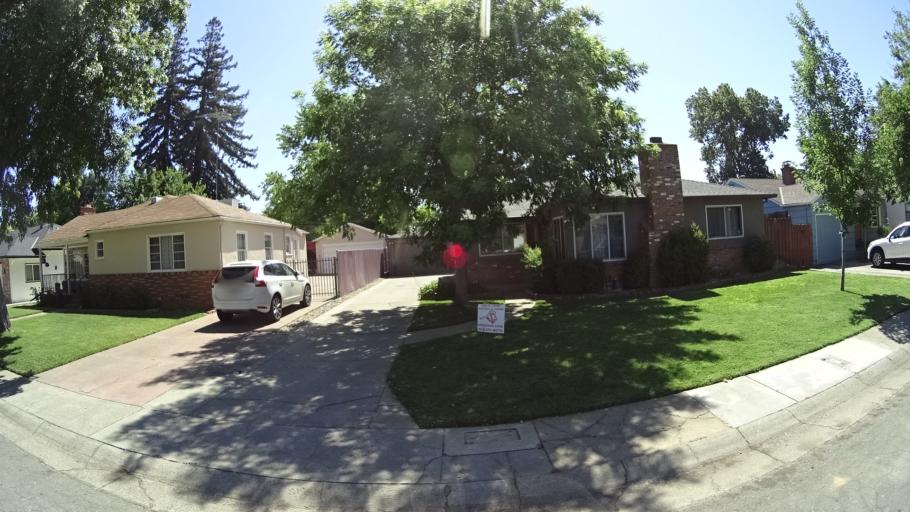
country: US
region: California
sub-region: Sacramento County
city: Parkway
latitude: 38.5268
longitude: -121.4912
